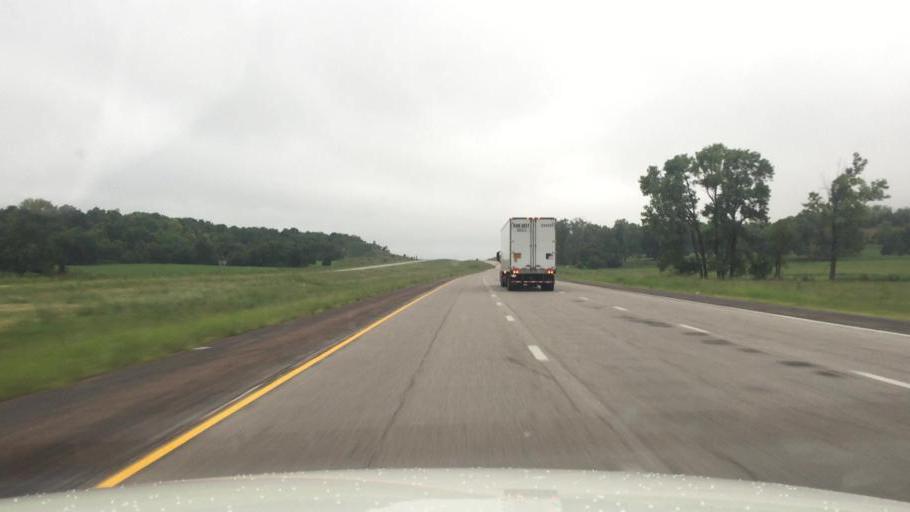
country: US
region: Kansas
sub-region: Montgomery County
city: Cherryvale
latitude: 37.2226
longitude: -95.5858
